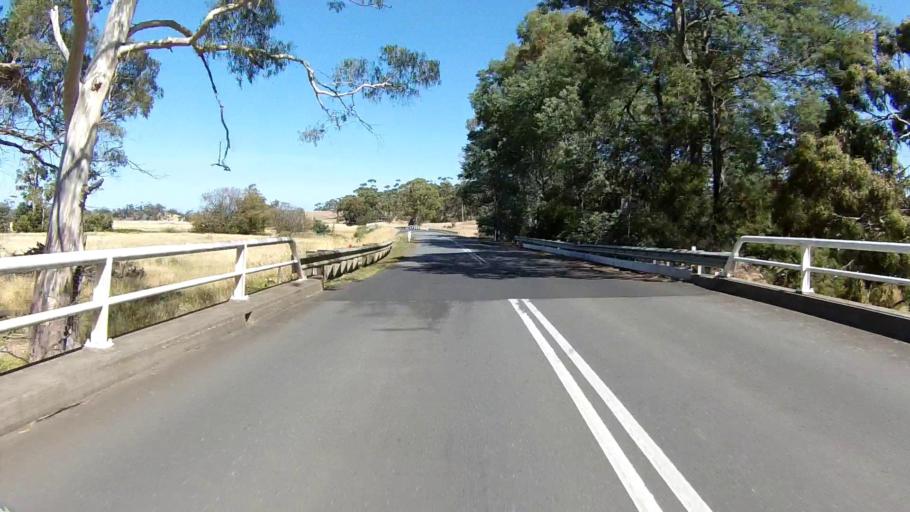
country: AU
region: Tasmania
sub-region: Sorell
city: Sorell
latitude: -42.2611
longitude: 148.0024
